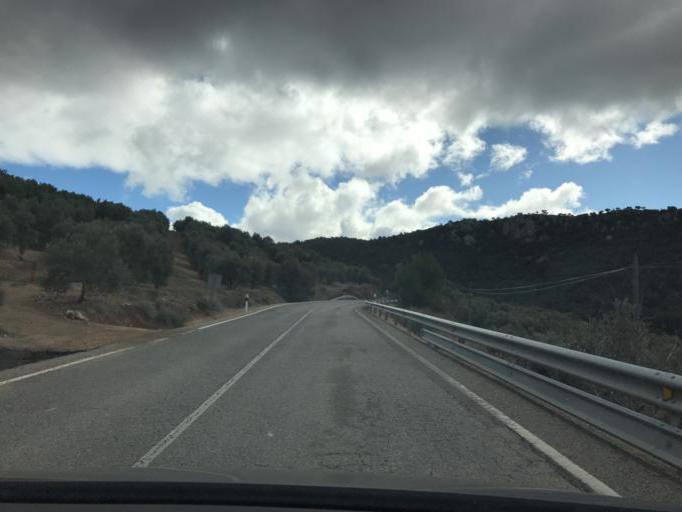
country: ES
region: Andalusia
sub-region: Provincia de Jaen
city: Cambil
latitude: 37.6929
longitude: -3.5087
